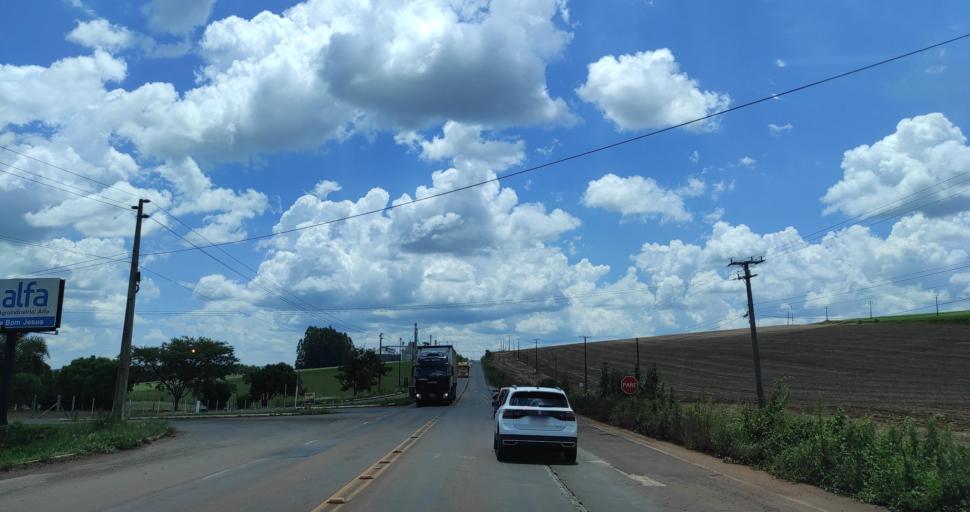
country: BR
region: Santa Catarina
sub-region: Xanxere
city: Xanxere
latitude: -26.7681
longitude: -52.4054
